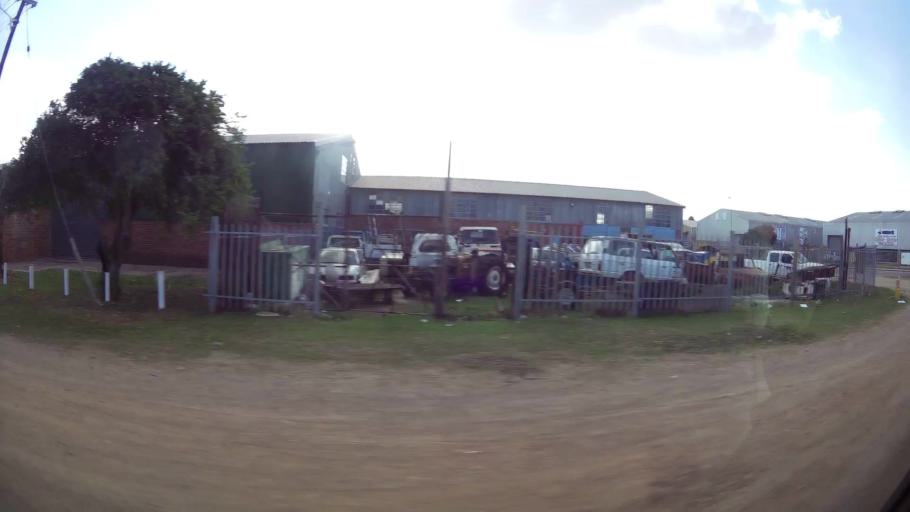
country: ZA
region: Eastern Cape
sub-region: Nelson Mandela Bay Metropolitan Municipality
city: Uitenhage
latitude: -33.7706
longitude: 25.3912
